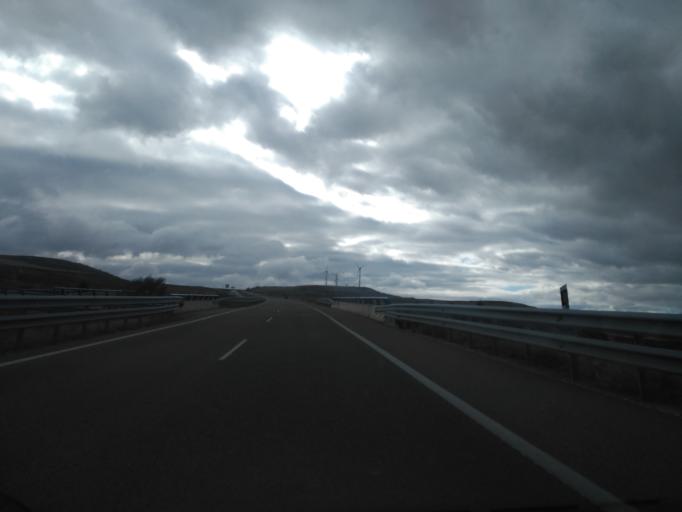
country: ES
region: Castille and Leon
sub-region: Provincia de Palencia
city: Monzon de Campos
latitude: 42.1193
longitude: -4.4808
